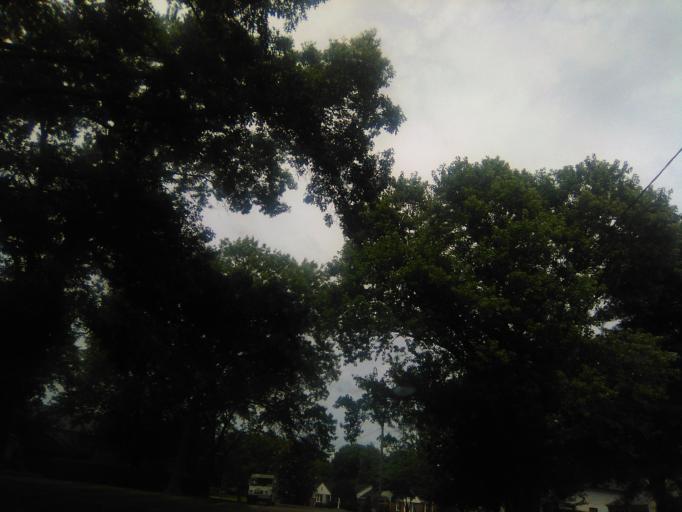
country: US
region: Tennessee
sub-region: Davidson County
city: Belle Meade
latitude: 36.1028
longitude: -86.8734
